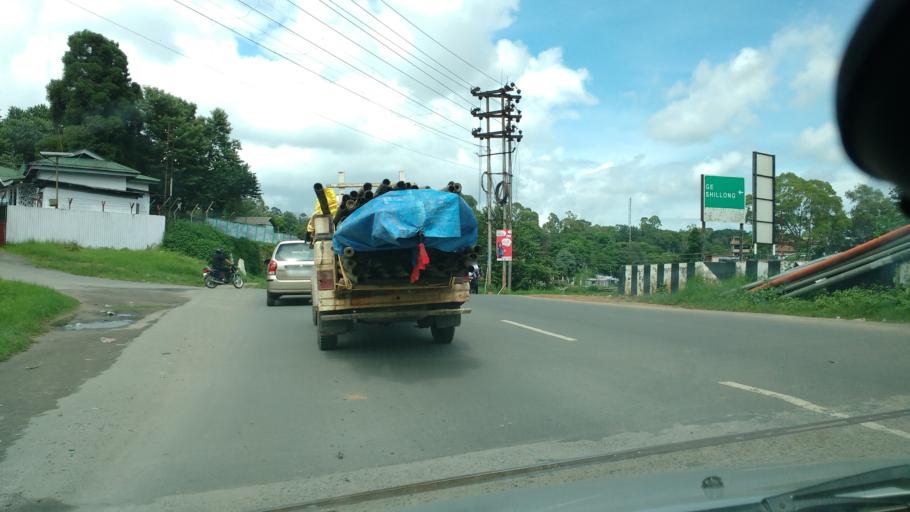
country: IN
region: Meghalaya
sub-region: East Khasi Hills
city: Shillong
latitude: 25.5714
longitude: 91.8686
